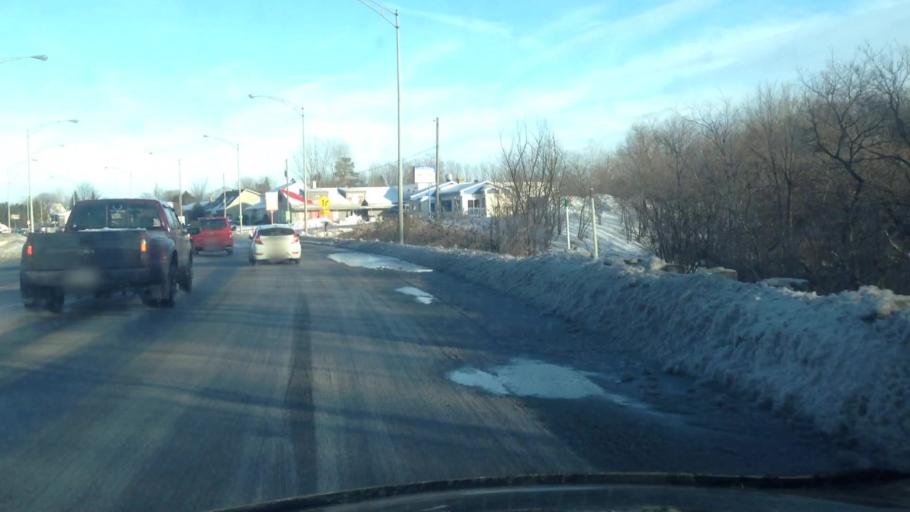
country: CA
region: Quebec
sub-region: Laurentides
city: Saint-Jerome
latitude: 45.7639
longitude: -73.9837
